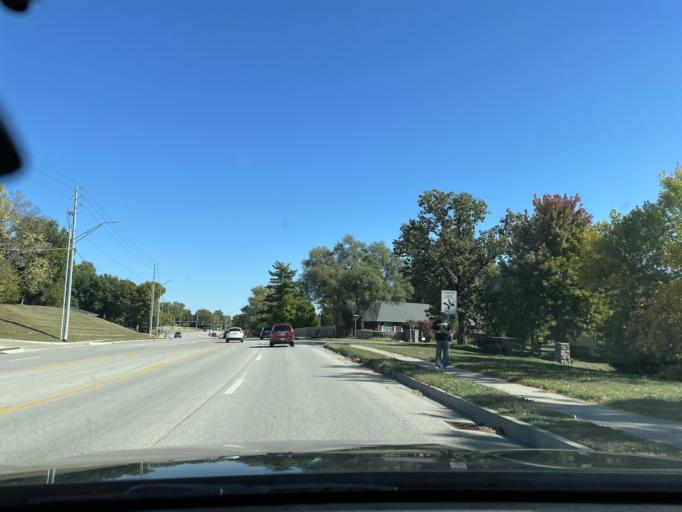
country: US
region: Missouri
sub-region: Buchanan County
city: Saint Joseph
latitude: 39.7771
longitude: -94.7903
